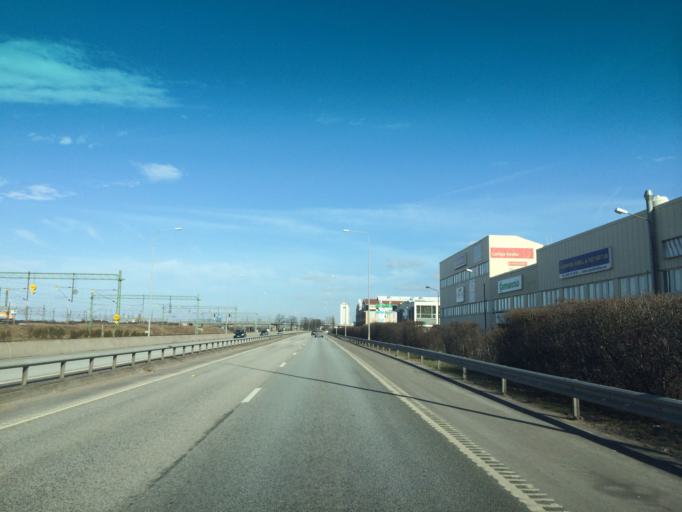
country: SE
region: Skane
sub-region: Malmo
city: Malmoe
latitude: 55.6121
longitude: 13.0344
